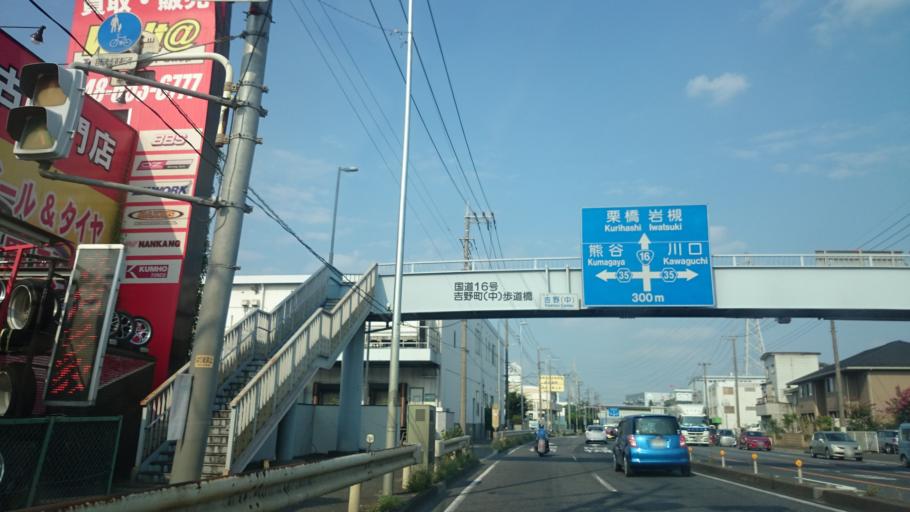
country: JP
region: Saitama
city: Ageoshimo
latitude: 35.9546
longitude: 139.6103
